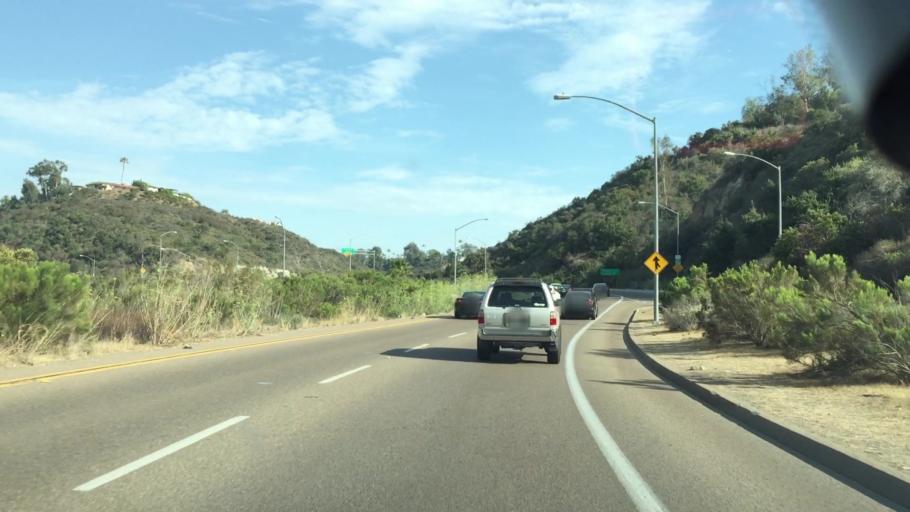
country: US
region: California
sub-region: San Diego County
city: Lemon Grove
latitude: 32.7743
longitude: -117.0983
